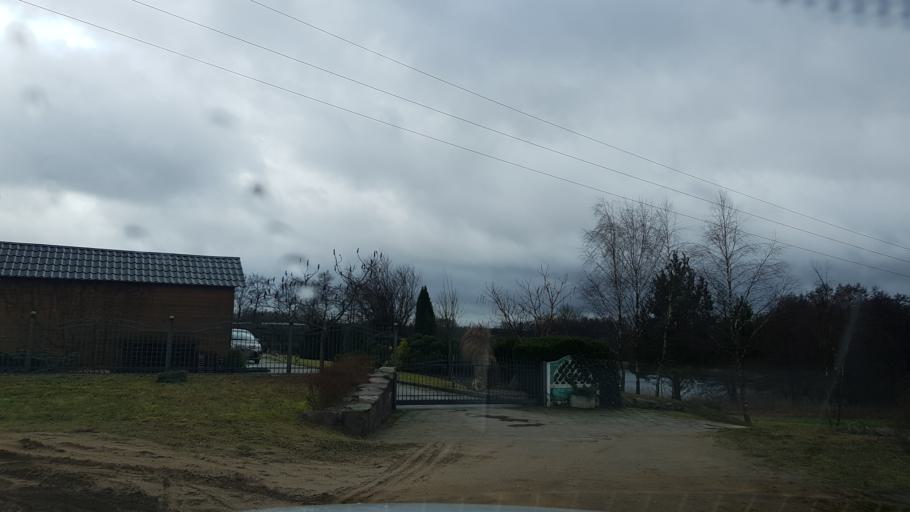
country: PL
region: West Pomeranian Voivodeship
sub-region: Powiat drawski
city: Czaplinek
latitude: 53.5500
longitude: 16.2492
